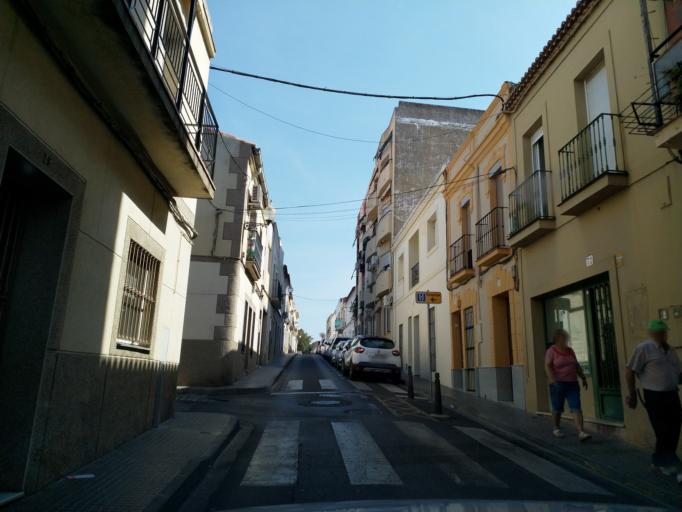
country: ES
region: Extremadura
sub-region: Provincia de Badajoz
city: Merida
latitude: 38.9159
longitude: -6.3410
